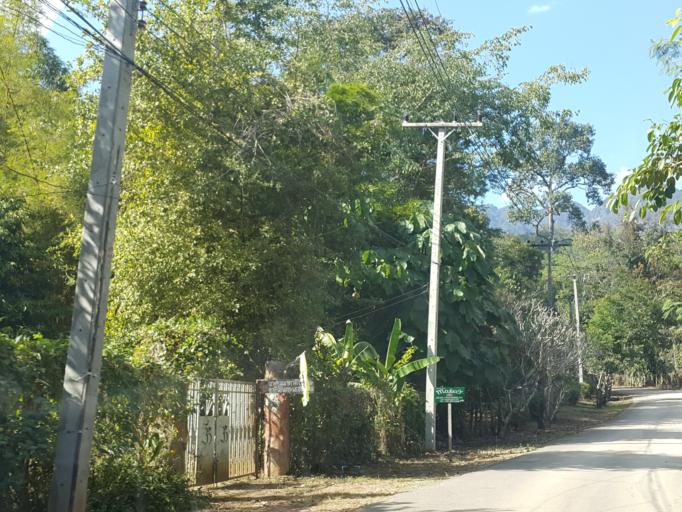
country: TH
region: Chiang Mai
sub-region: Amphoe Chiang Dao
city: Chiang Dao
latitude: 19.4026
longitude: 98.9263
